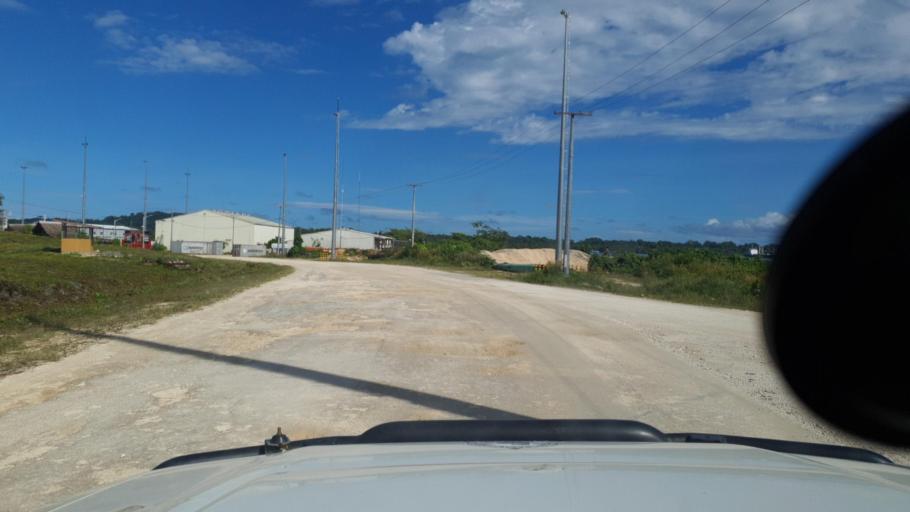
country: SB
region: Western Province
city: Gizo
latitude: -8.2332
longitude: 157.1997
